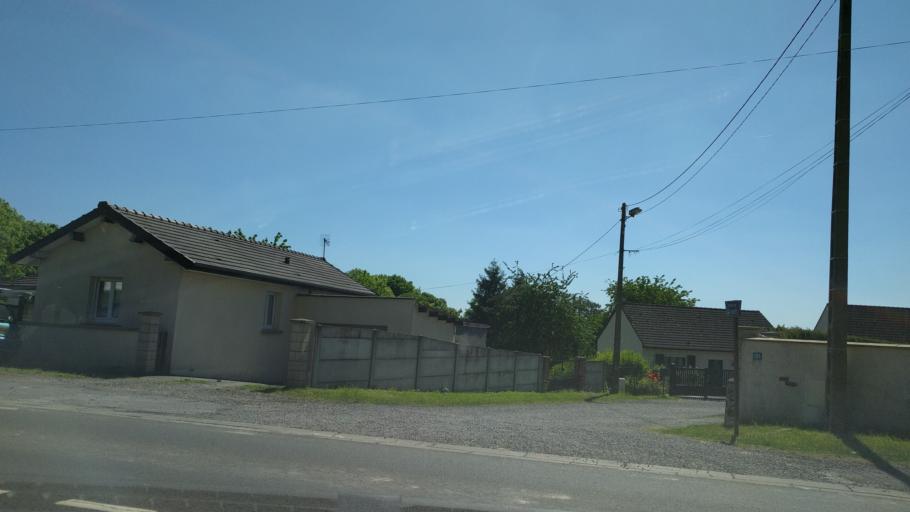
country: FR
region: Picardie
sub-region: Departement de la Somme
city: Peronne
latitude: 49.9472
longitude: 2.9333
